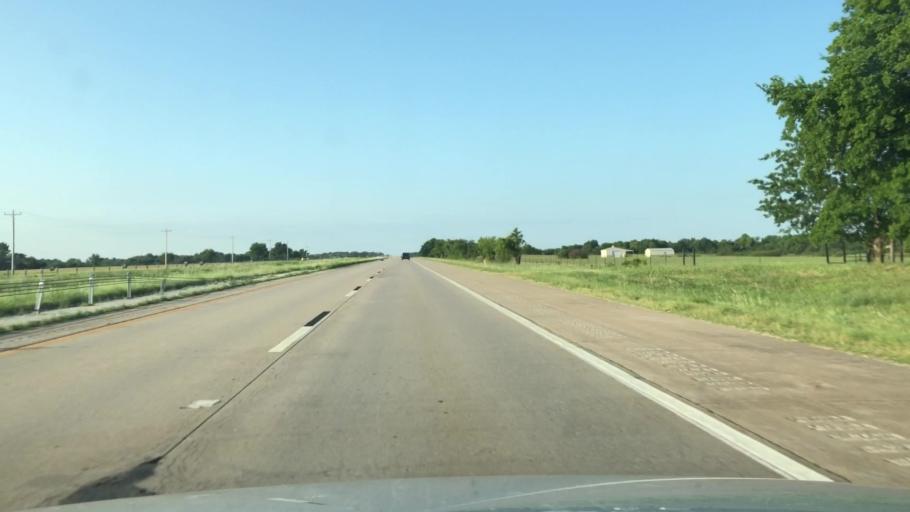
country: US
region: Oklahoma
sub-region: Osage County
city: Skiatook
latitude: 36.4493
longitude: -95.9207
